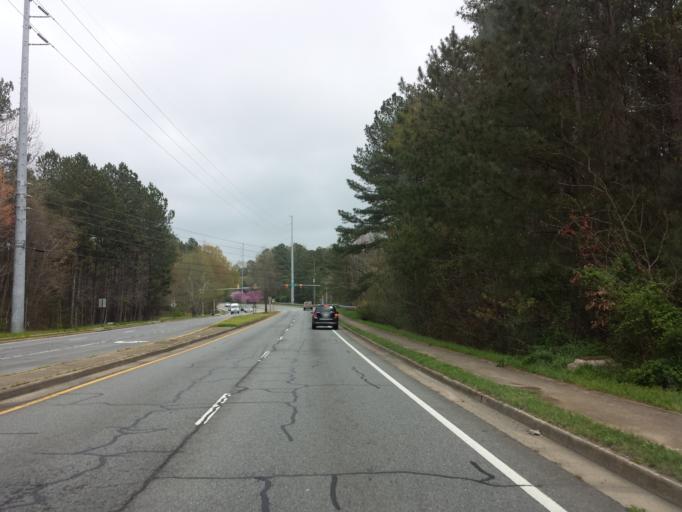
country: US
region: Georgia
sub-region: Cherokee County
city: Woodstock
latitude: 34.0268
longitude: -84.4741
